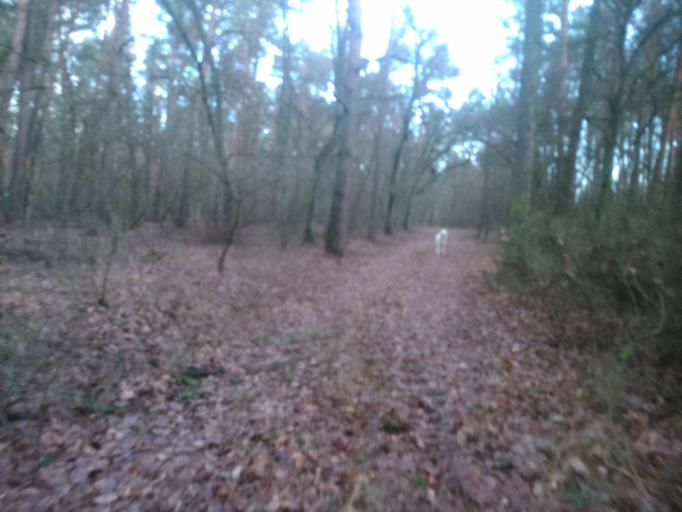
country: PL
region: Kujawsko-Pomorskie
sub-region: Powiat golubsko-dobrzynski
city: Golub-Dobrzyn
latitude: 53.1357
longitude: 19.1293
